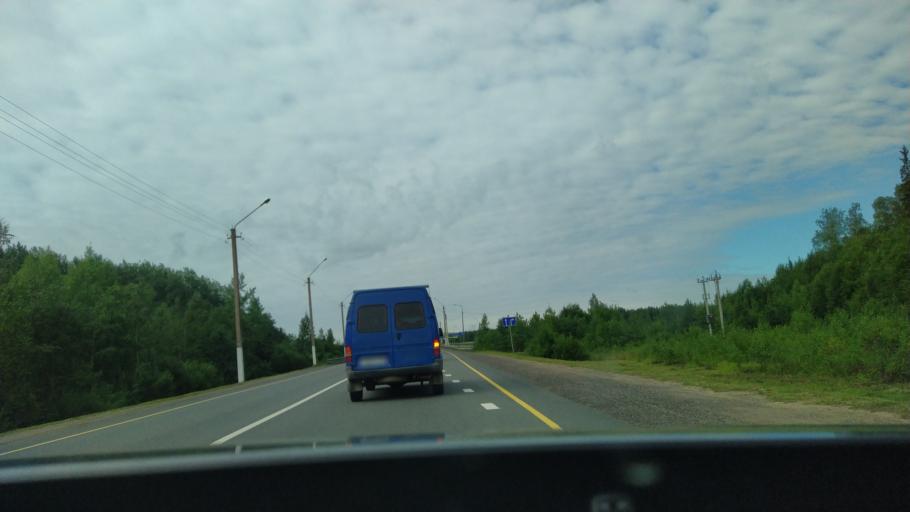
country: RU
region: Leningrad
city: Ul'yanovka
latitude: 59.6083
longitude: 30.7648
